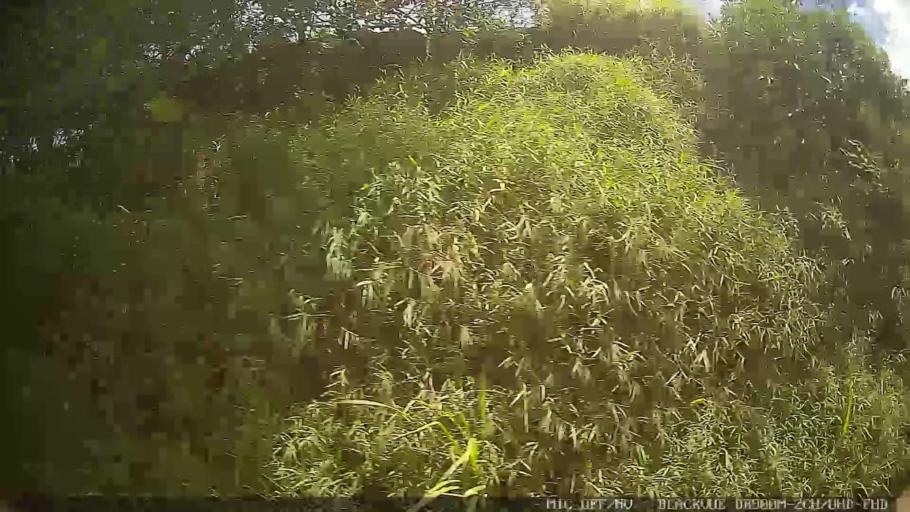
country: BR
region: Minas Gerais
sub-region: Extrema
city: Extrema
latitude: -22.7295
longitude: -46.3848
